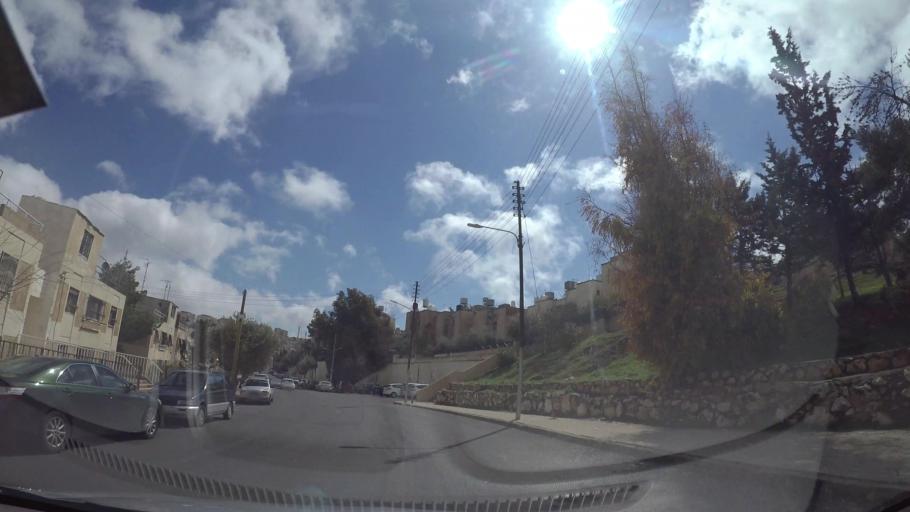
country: JO
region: Amman
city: Al Jubayhah
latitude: 32.0585
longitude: 35.8812
